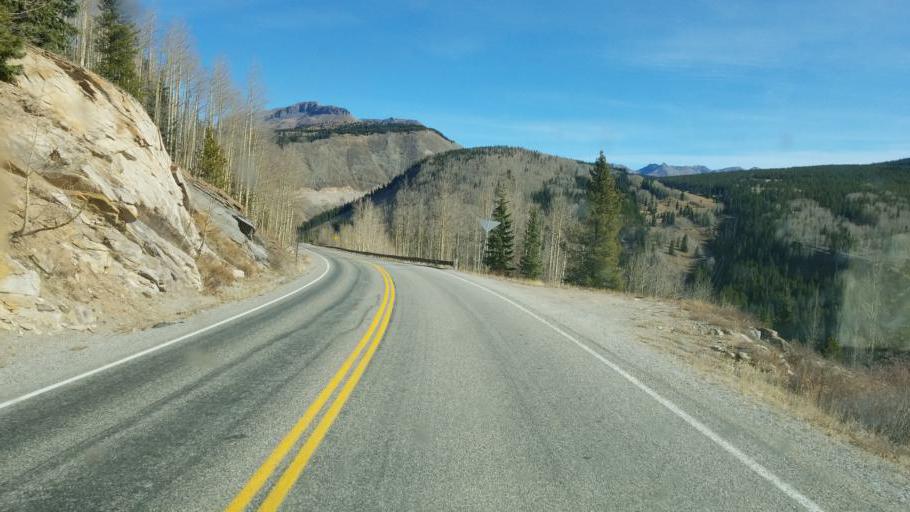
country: US
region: Colorado
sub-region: San Juan County
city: Silverton
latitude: 37.7126
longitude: -107.7567
